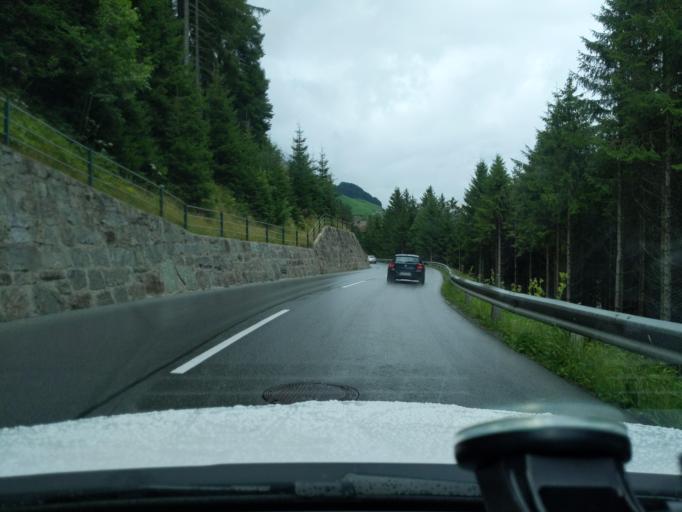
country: AT
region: Tyrol
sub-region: Politischer Bezirk Innsbruck Land
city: Schmirn
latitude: 47.1247
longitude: 11.6928
